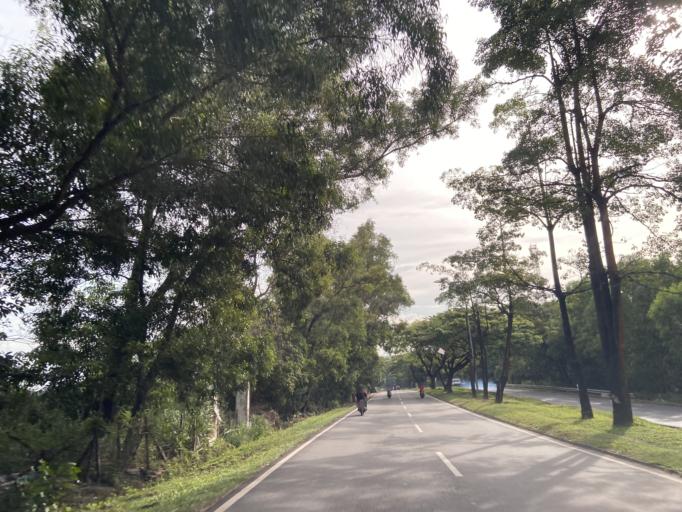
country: SG
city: Singapore
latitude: 1.1461
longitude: 104.0218
